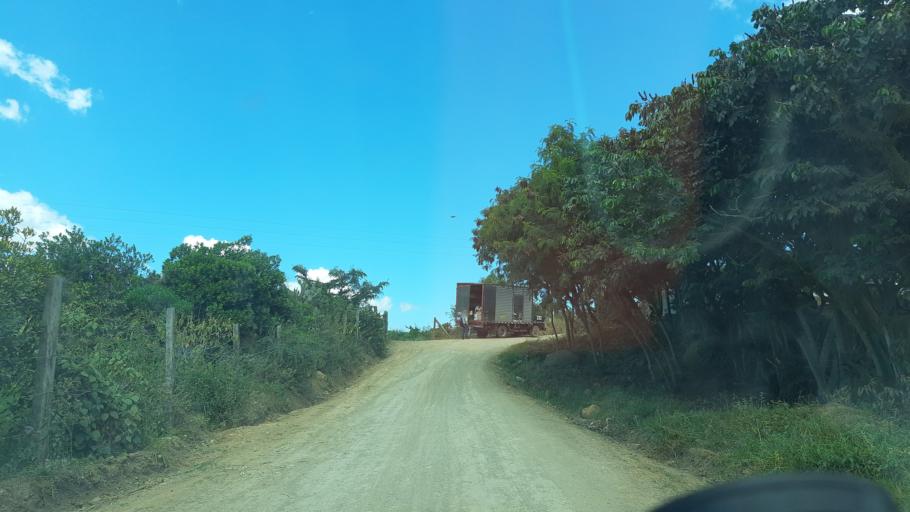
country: CO
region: Boyaca
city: Villa de Leiva
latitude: 5.6682
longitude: -73.5735
